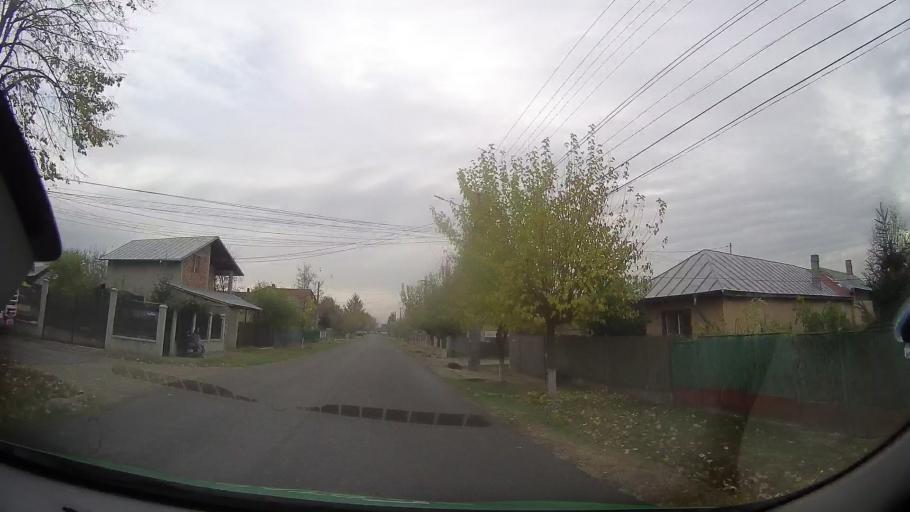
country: RO
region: Prahova
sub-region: Comuna Valea Calugareasca
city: Pantazi
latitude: 44.9377
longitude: 26.1369
